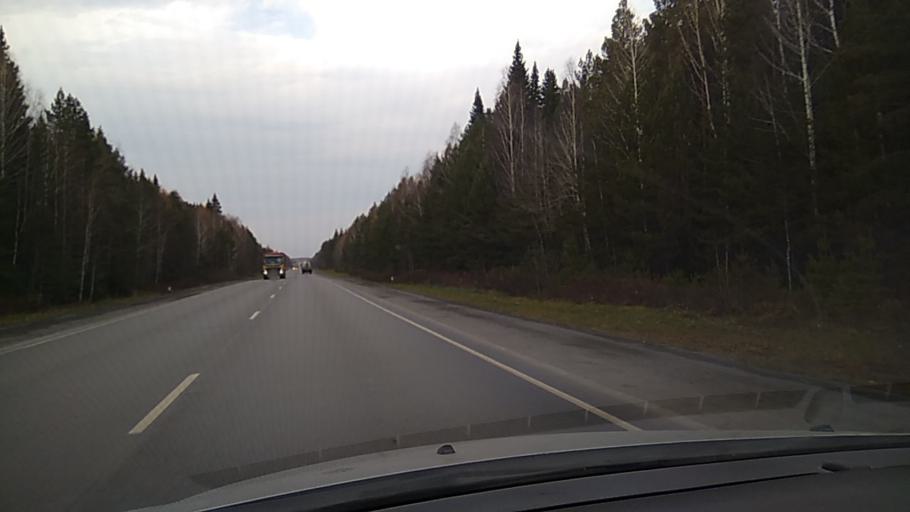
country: RU
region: Sverdlovsk
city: Tugulym
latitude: 57.0717
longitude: 64.6160
